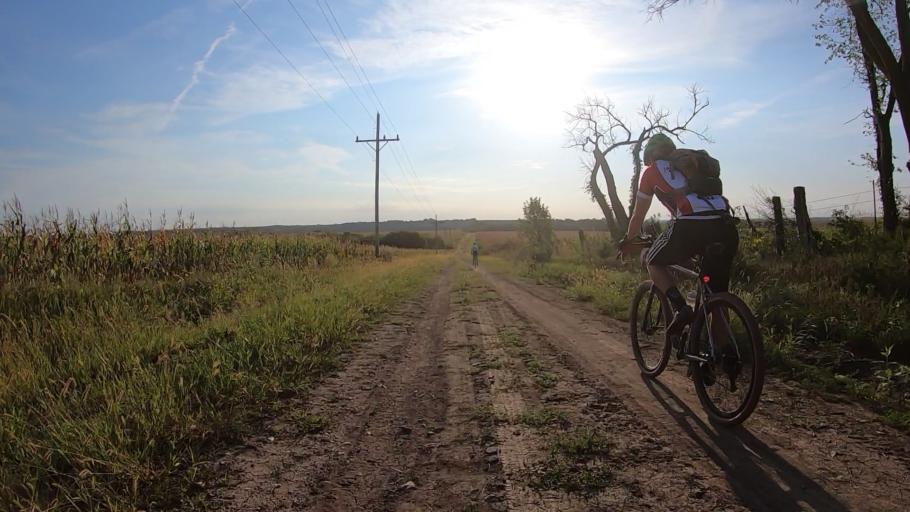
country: US
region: Kansas
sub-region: Marshall County
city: Blue Rapids
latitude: 39.7117
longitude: -96.7914
